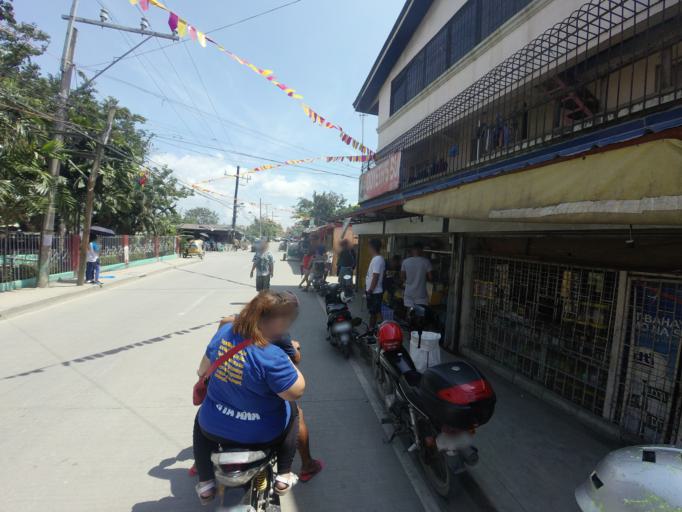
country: PH
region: Calabarzon
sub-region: Province of Rizal
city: Taytay
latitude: 14.5428
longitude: 121.1087
